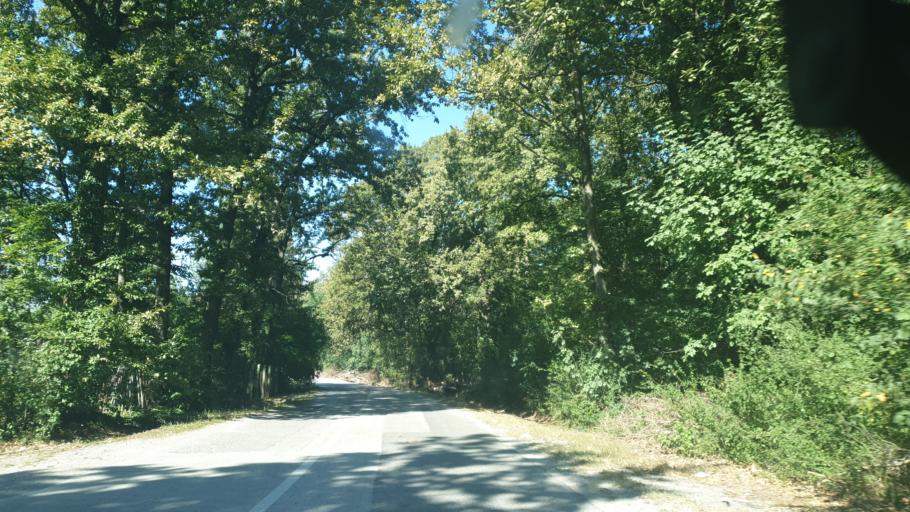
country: RS
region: Central Serbia
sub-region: Kolubarski Okrug
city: Lajkovac
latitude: 44.3091
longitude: 20.1672
